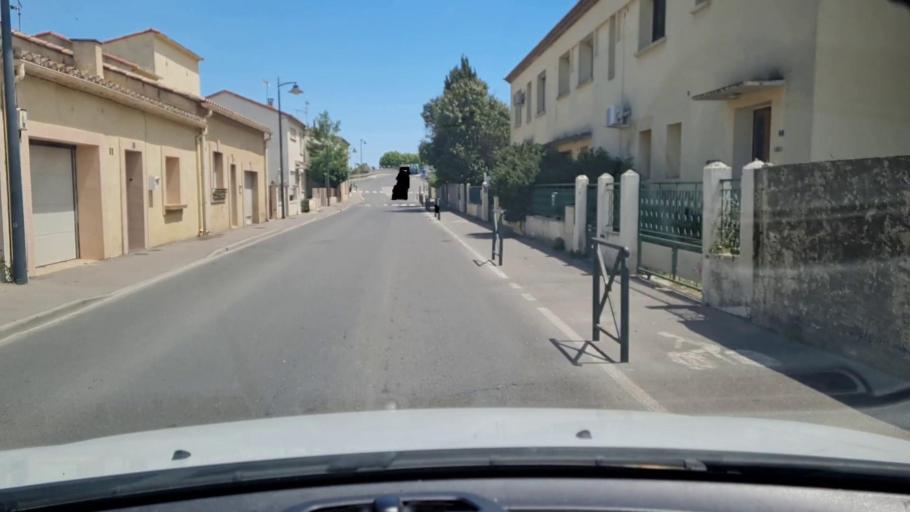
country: FR
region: Languedoc-Roussillon
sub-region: Departement du Gard
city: Aigues-Mortes
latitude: 43.5691
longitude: 4.1874
